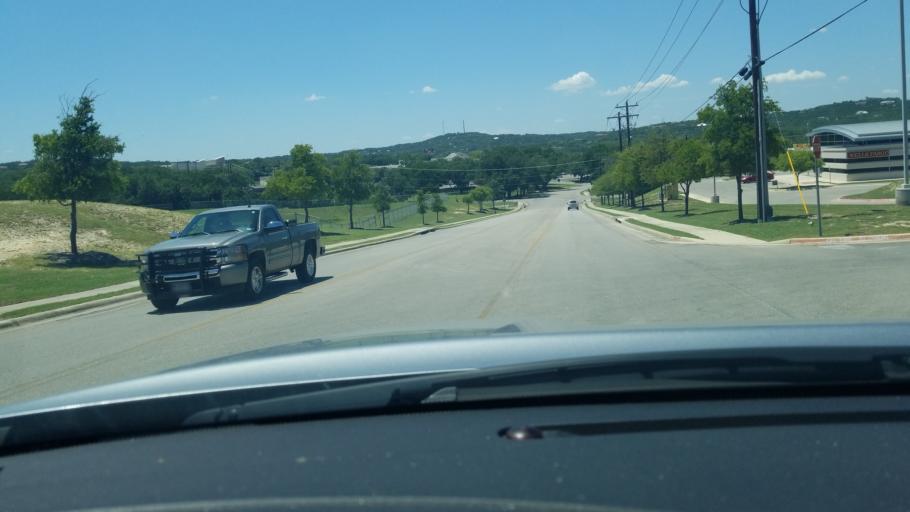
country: US
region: Texas
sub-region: Comal County
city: Bulverde
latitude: 29.7952
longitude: -98.4235
